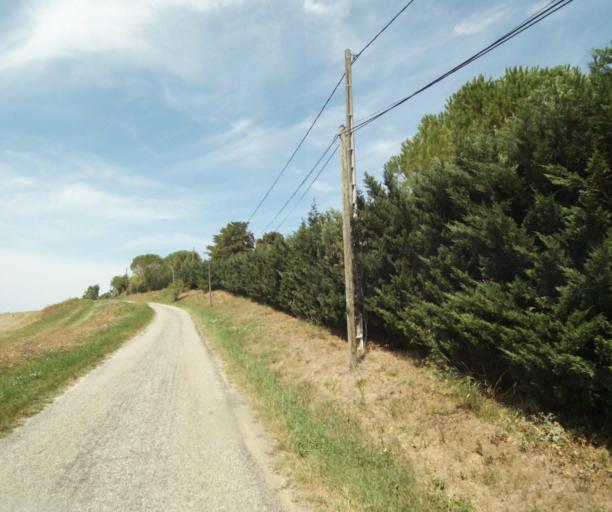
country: FR
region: Midi-Pyrenees
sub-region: Departement de l'Ariege
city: Lezat-sur-Leze
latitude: 43.2395
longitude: 1.3788
